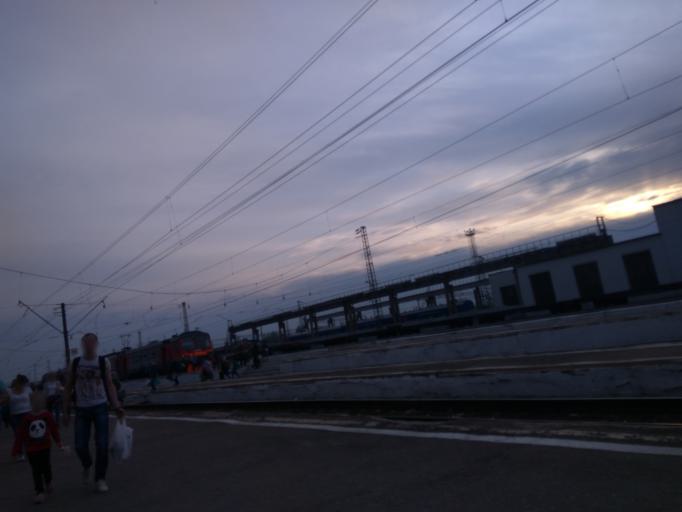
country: RU
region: Vladimir
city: Aleksandrov
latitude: 56.3983
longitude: 38.7048
